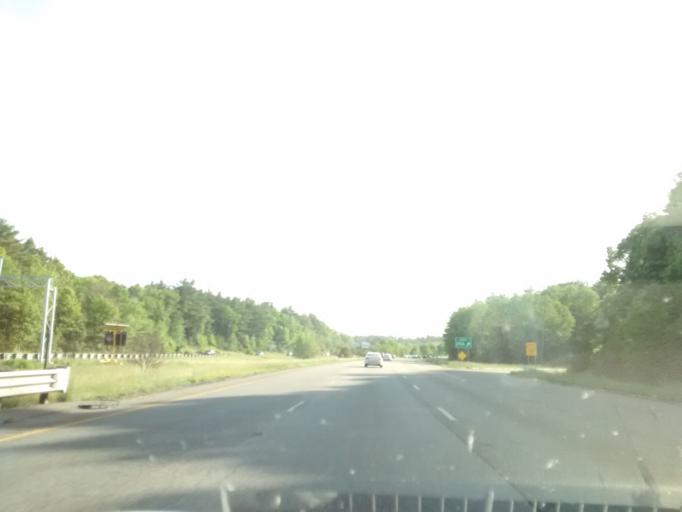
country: US
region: Massachusetts
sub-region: Worcester County
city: Northborough
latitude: 42.3468
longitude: -71.6243
